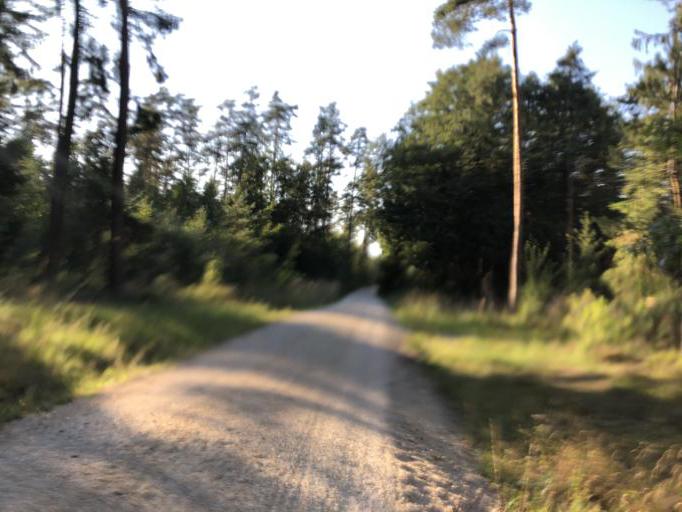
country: DE
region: Bavaria
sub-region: Regierungsbezirk Mittelfranken
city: Uttenreuth
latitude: 49.5727
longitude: 11.0816
